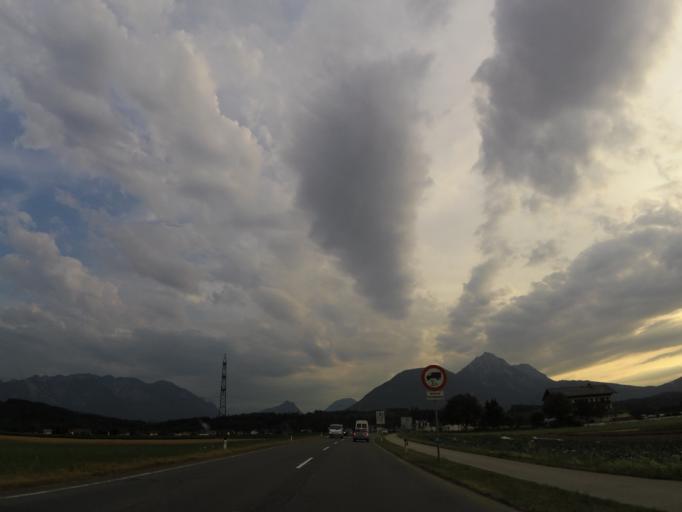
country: DE
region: Bavaria
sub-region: Upper Bavaria
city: Ainring
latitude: 47.7813
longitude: 12.9647
